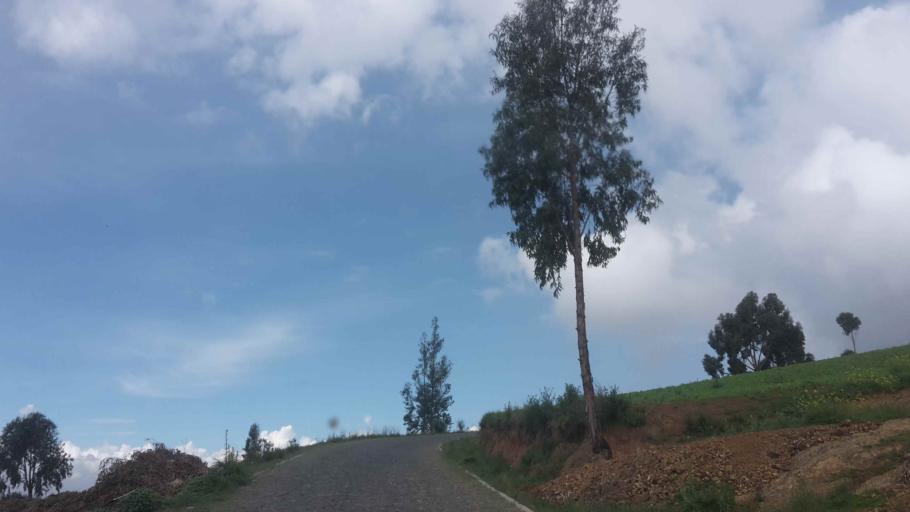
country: BO
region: Cochabamba
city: Cochabamba
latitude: -17.3571
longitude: -66.0555
